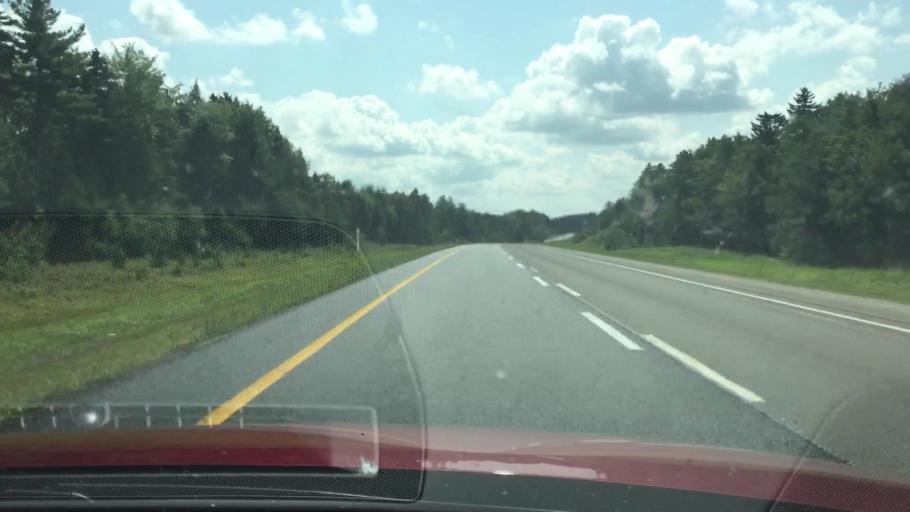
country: US
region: Maine
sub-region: Penobscot County
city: Medway
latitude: 45.6908
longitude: -68.4885
